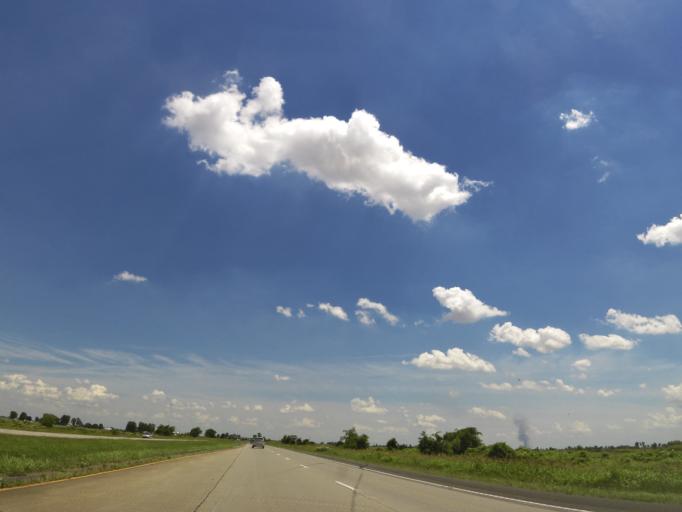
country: US
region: Missouri
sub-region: Pemiscot County
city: Hayti
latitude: 36.2103
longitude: -89.7417
